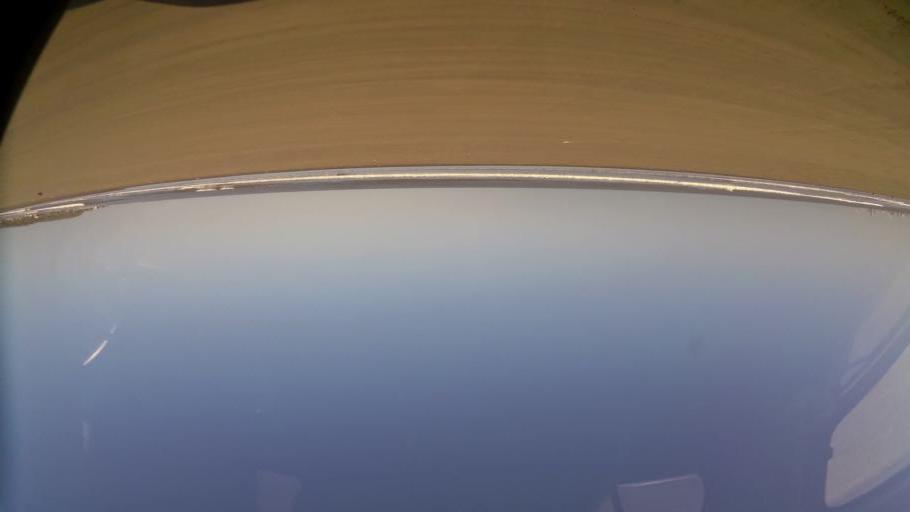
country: CO
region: Bolivar
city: Cartagena
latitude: 10.4878
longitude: -75.4920
